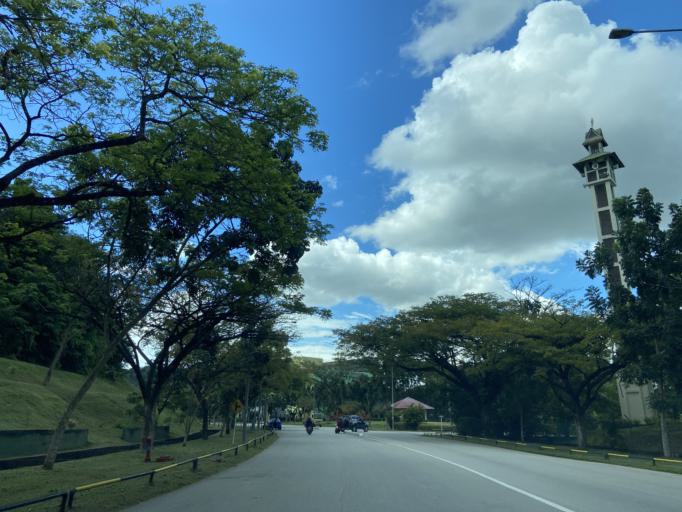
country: SG
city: Singapore
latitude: 1.0657
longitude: 104.0248
